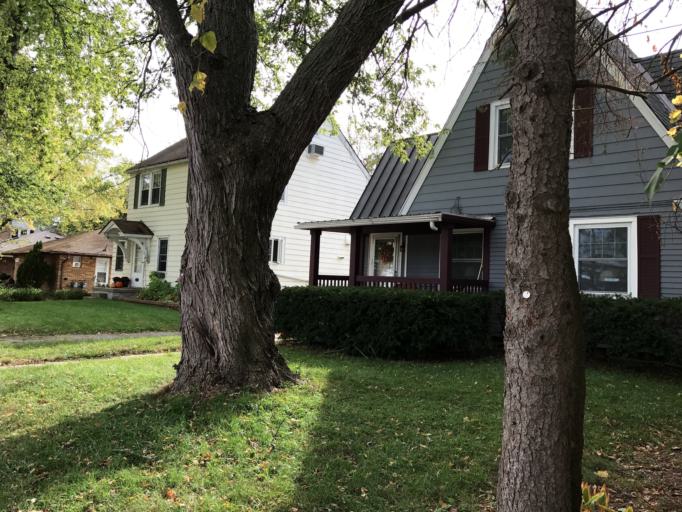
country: US
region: Michigan
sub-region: Washtenaw County
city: Ann Arbor
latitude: 42.2566
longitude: -83.7272
